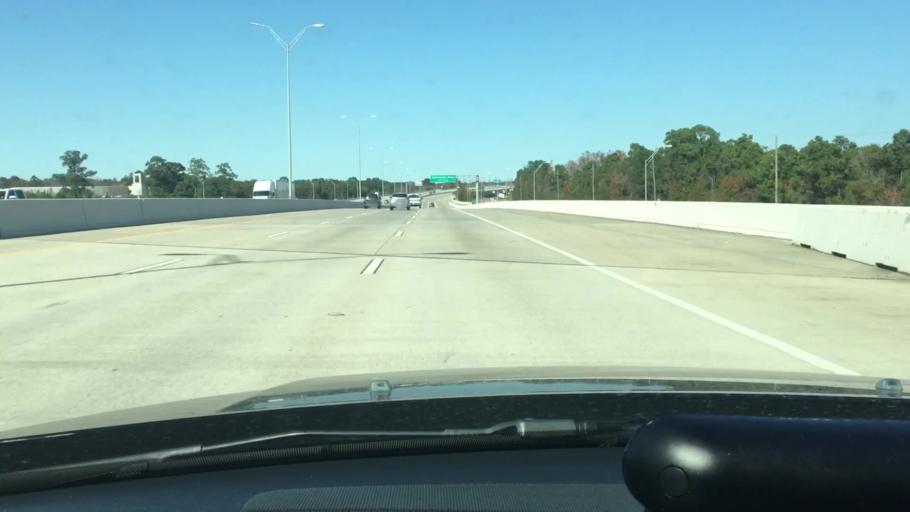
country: US
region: Texas
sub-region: Harris County
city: Sheldon
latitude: 29.8835
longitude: -95.1980
